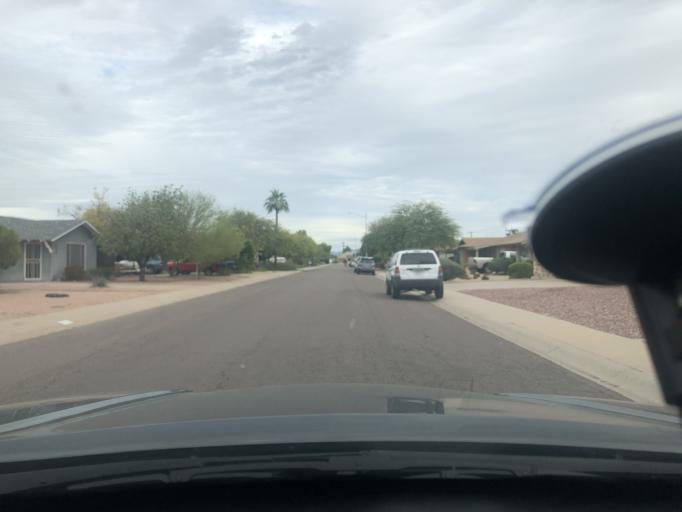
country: US
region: Arizona
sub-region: Maricopa County
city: Scottsdale
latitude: 33.4905
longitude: -111.9038
